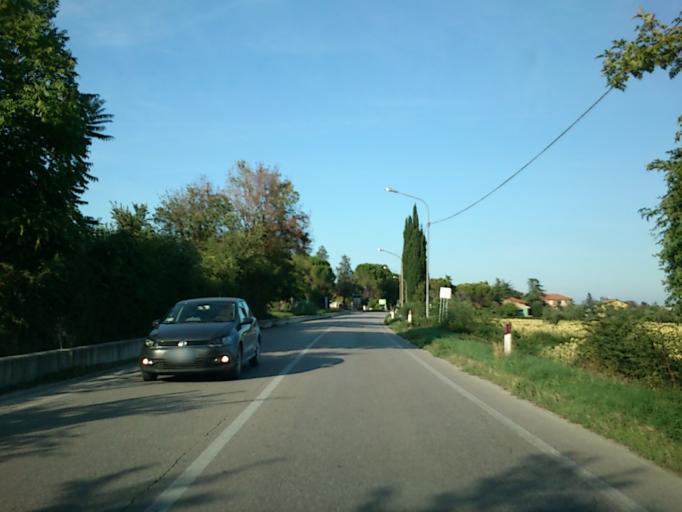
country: IT
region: The Marches
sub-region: Provincia di Pesaro e Urbino
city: Fossombrone
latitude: 43.6992
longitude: 12.8294
